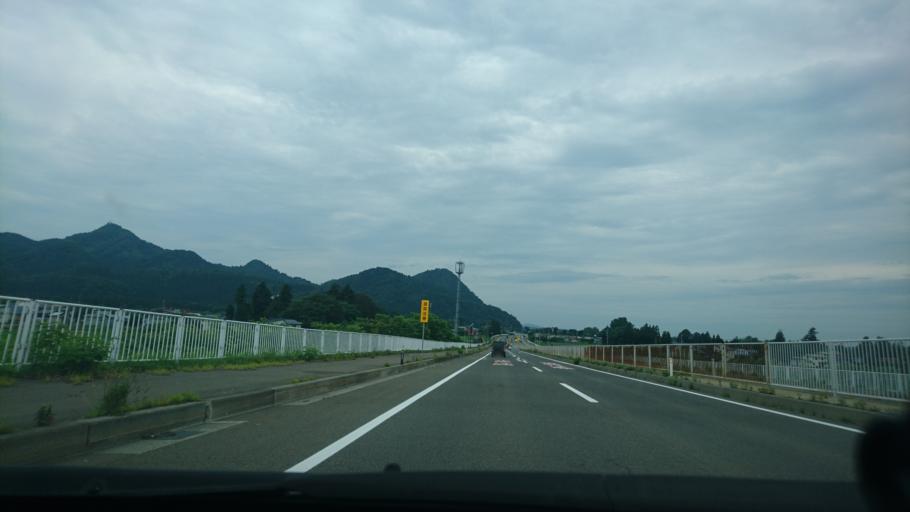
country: JP
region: Akita
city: Omagari
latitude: 39.4769
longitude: 140.4659
